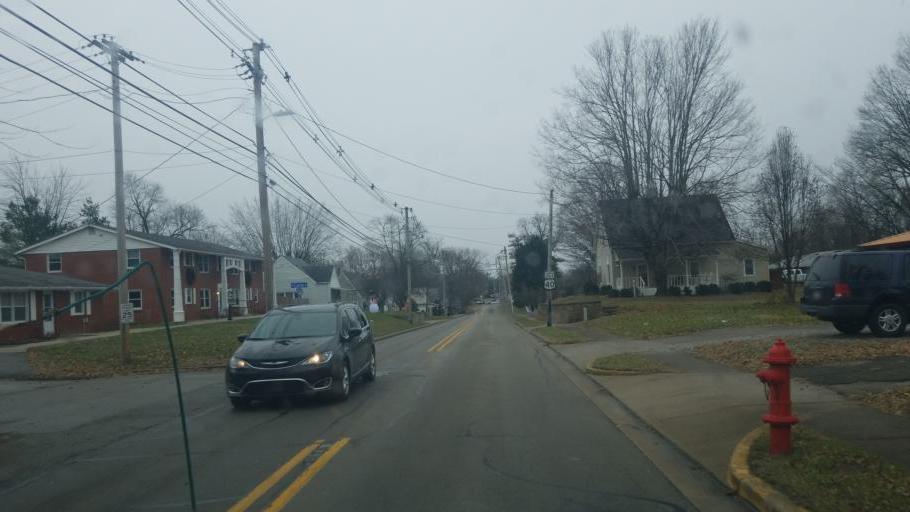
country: US
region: Indiana
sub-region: Henry County
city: Knightstown
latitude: 39.7982
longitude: -85.5322
